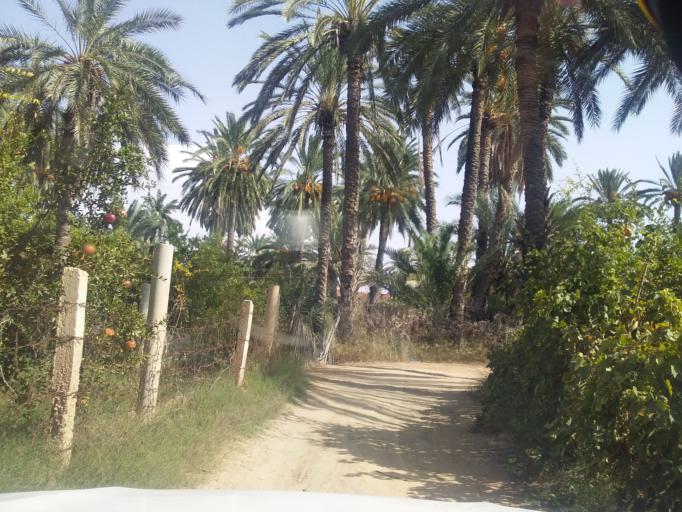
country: TN
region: Qabis
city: Gabes
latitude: 33.6246
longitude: 10.2873
